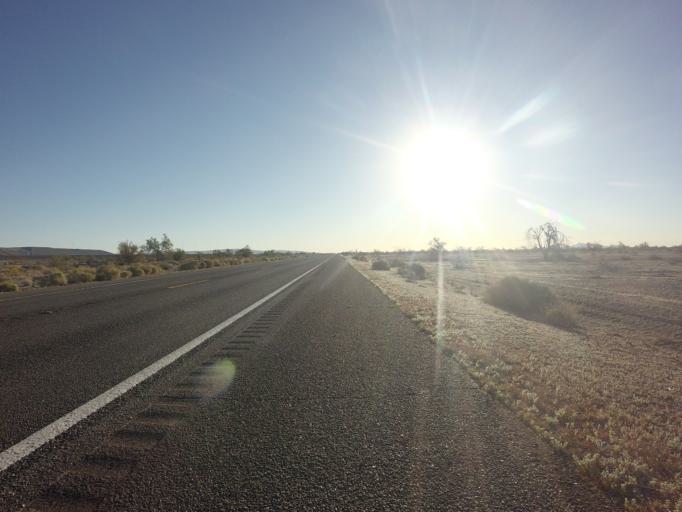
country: MX
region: Baja California
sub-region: Mexicali
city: Ejido Netzahualcoyotl
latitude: 33.0150
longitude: -115.0062
